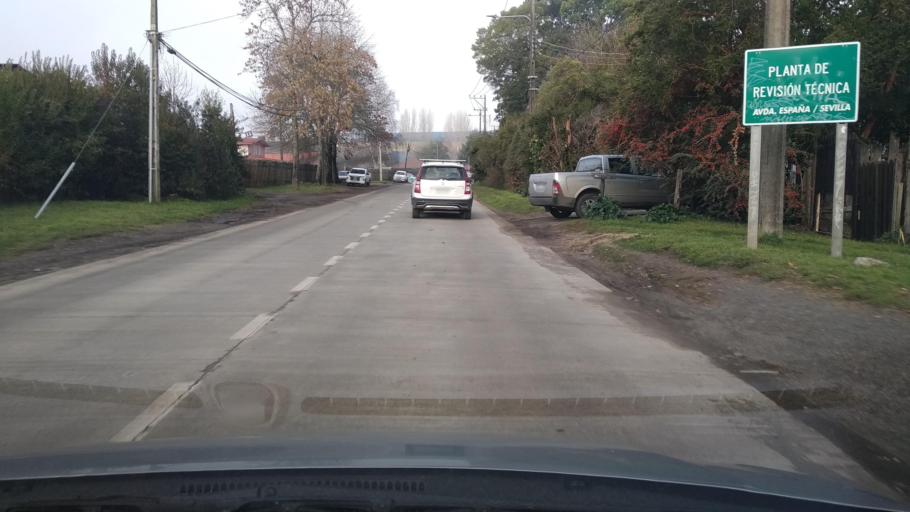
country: CL
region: Los Rios
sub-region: Provincia de Valdivia
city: Valdivia
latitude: -39.8047
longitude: -73.2395
